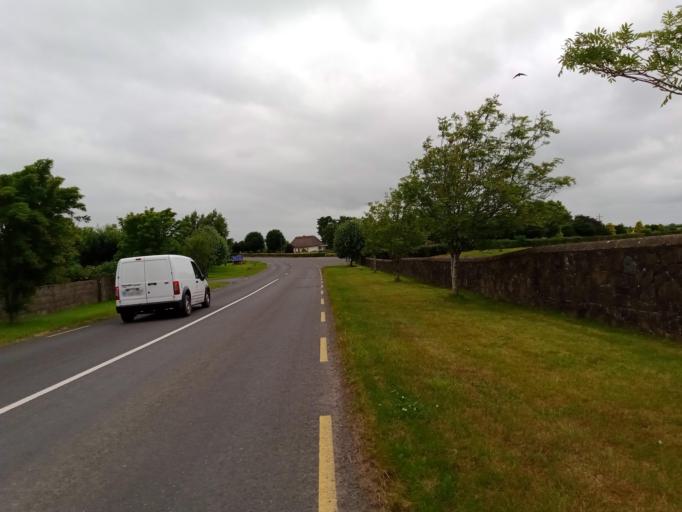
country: IE
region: Leinster
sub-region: Kilkenny
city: Callan
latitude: 52.5511
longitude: -7.3966
